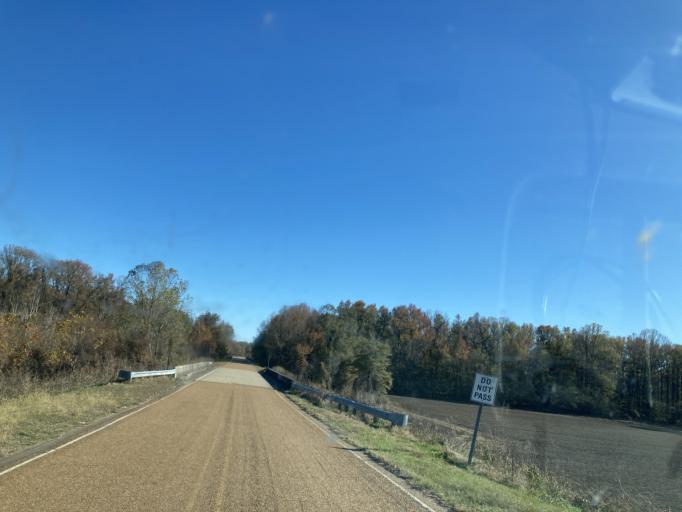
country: US
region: Mississippi
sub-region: Yazoo County
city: Yazoo City
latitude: 32.7757
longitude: -90.6370
